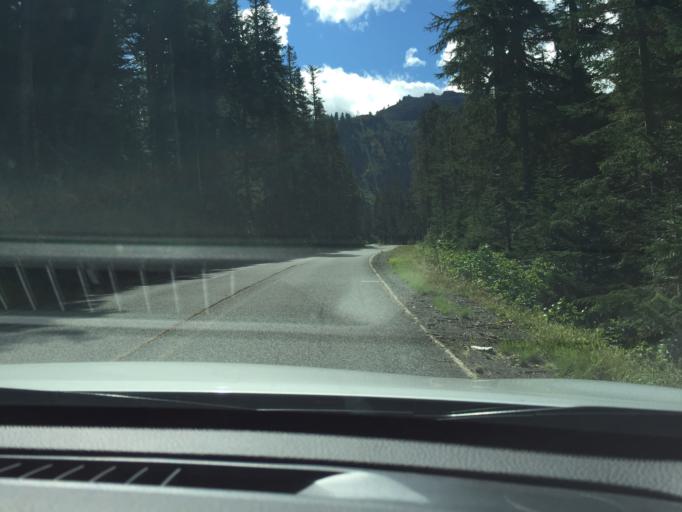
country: CA
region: British Columbia
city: Agassiz
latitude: 48.8639
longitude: -121.6558
